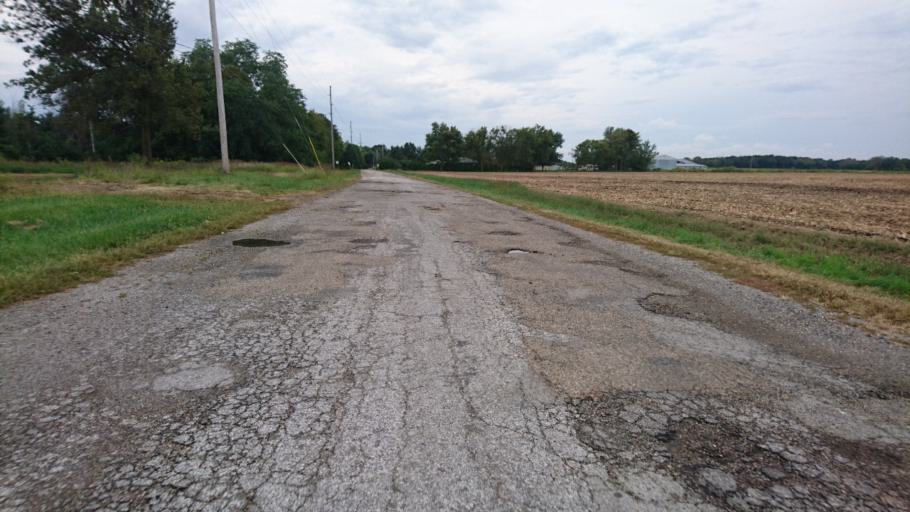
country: US
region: Illinois
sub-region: Sangamon County
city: Southern View
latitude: 39.7183
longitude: -89.6813
